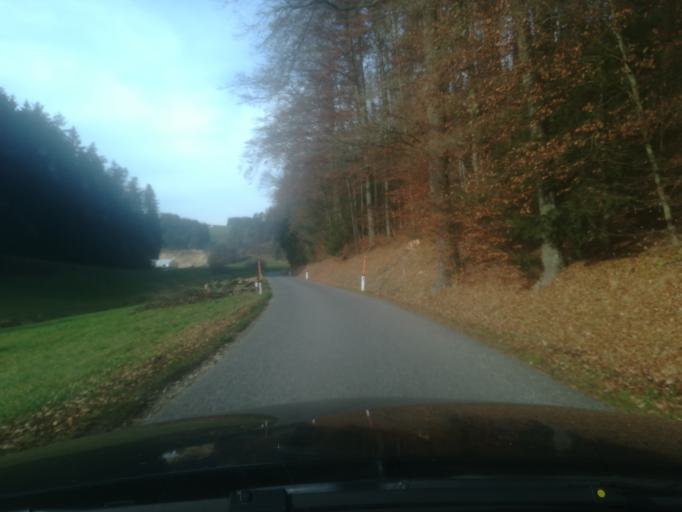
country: AT
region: Upper Austria
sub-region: Politischer Bezirk Perg
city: Perg
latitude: 48.3373
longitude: 14.6462
